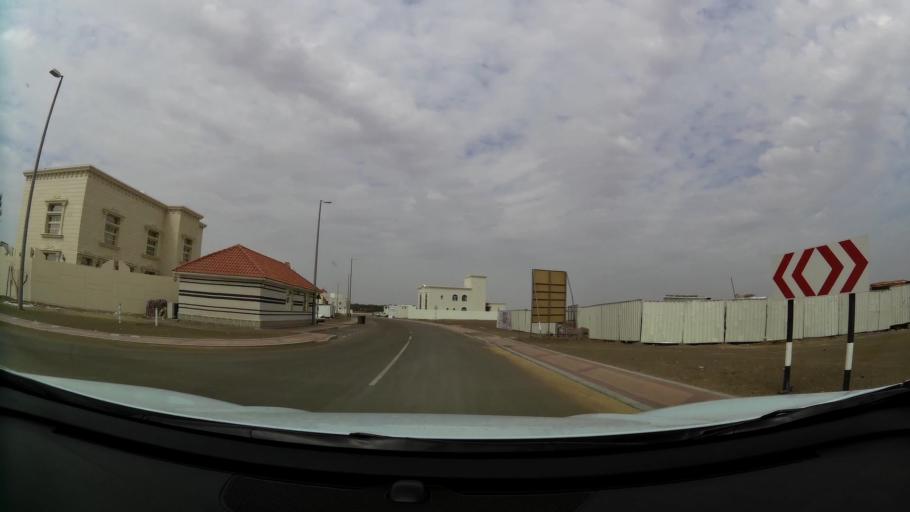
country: AE
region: Abu Dhabi
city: Al Ain
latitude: 24.1898
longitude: 55.8192
